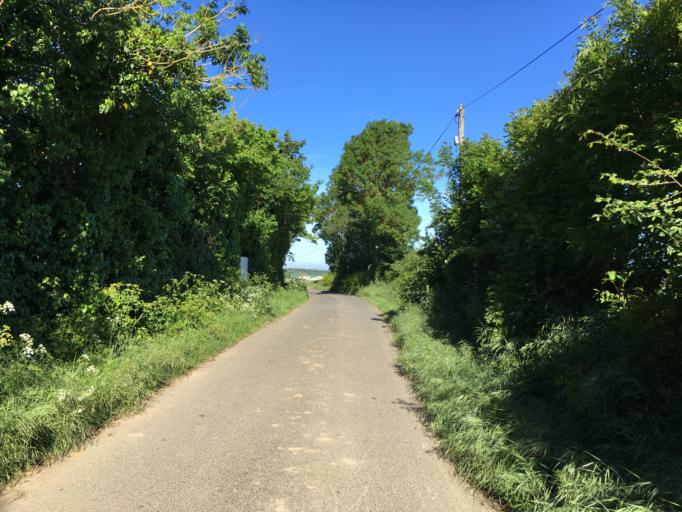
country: FR
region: Poitou-Charentes
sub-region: Departement de la Charente-Maritime
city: Lagord
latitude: 46.1823
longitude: -1.1762
